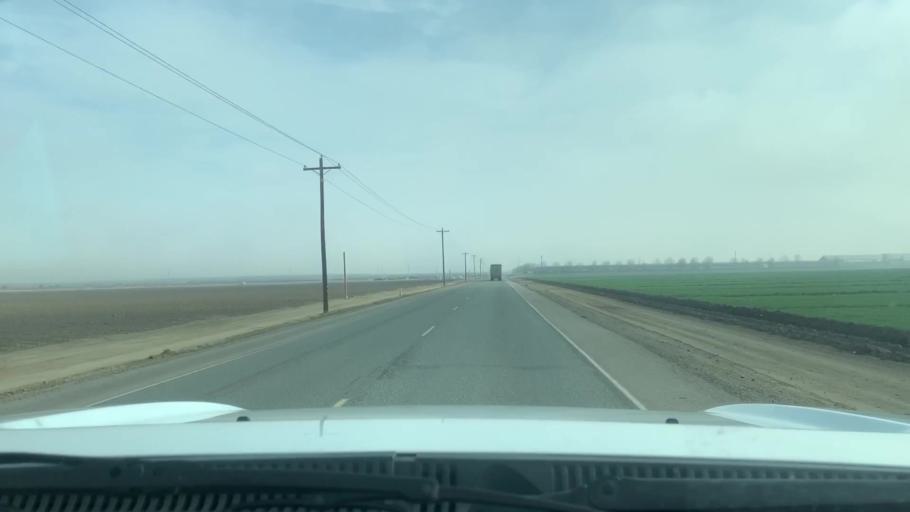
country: US
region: California
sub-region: Kern County
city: Buttonwillow
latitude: 35.5005
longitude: -119.4623
